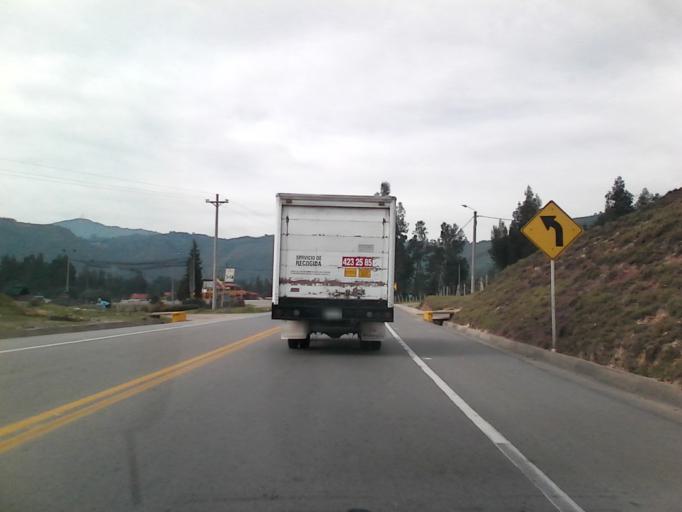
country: CO
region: Boyaca
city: Tibasosa
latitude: 5.7877
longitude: -72.9957
